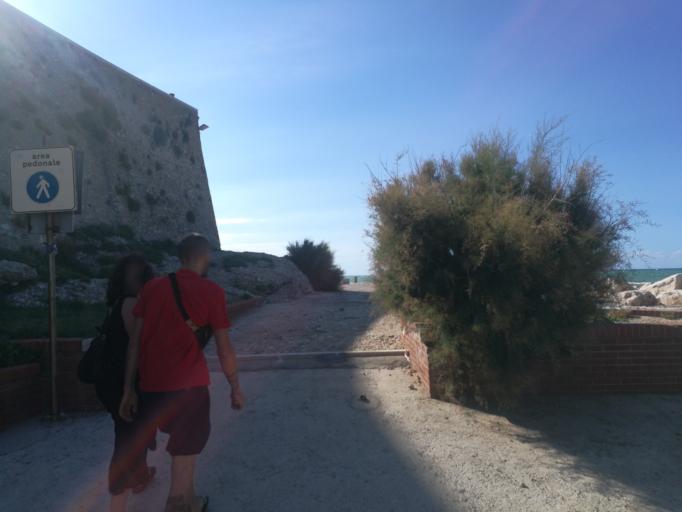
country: IT
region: Molise
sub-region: Provincia di Campobasso
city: Termoli
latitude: 42.0057
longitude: 14.9983
